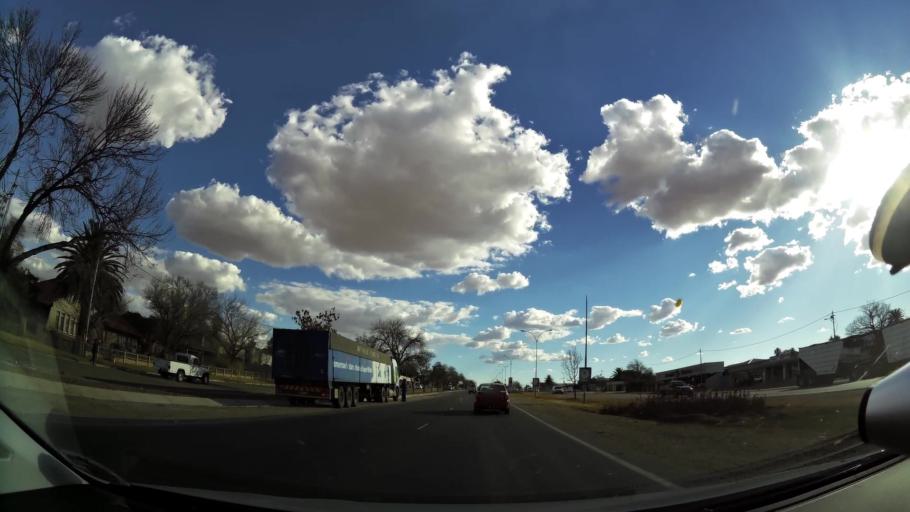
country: ZA
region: North-West
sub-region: Dr Kenneth Kaunda District Municipality
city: Klerksdorp
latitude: -26.8651
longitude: 26.6430
